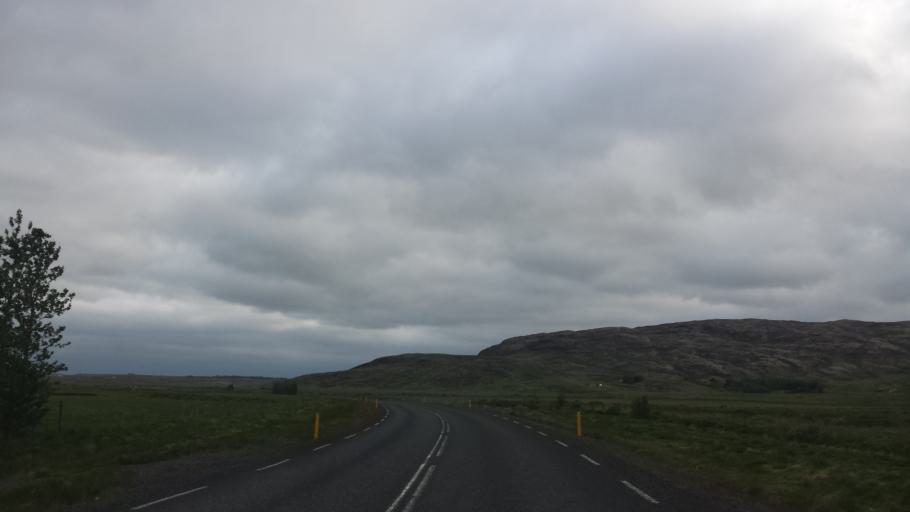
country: IS
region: South
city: Selfoss
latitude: 64.1428
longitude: -20.5641
